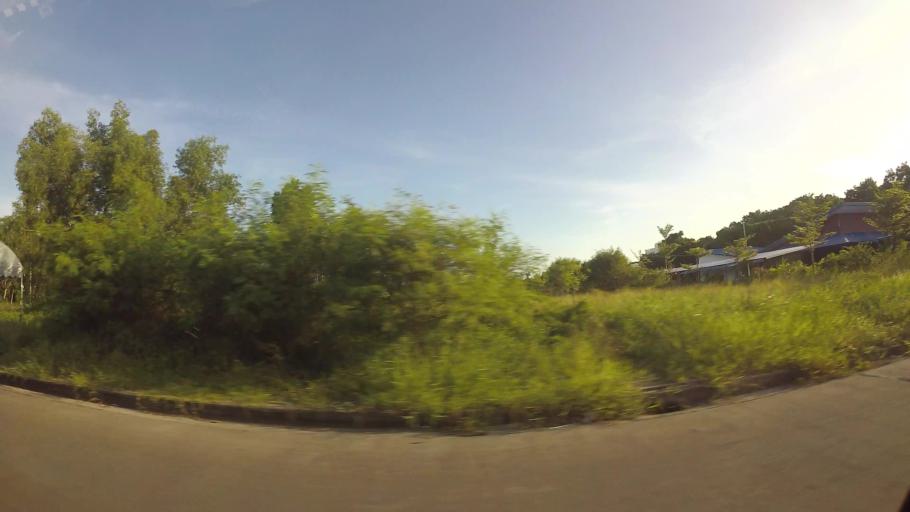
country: TH
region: Rayong
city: Rayong
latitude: 12.6865
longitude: 101.2814
